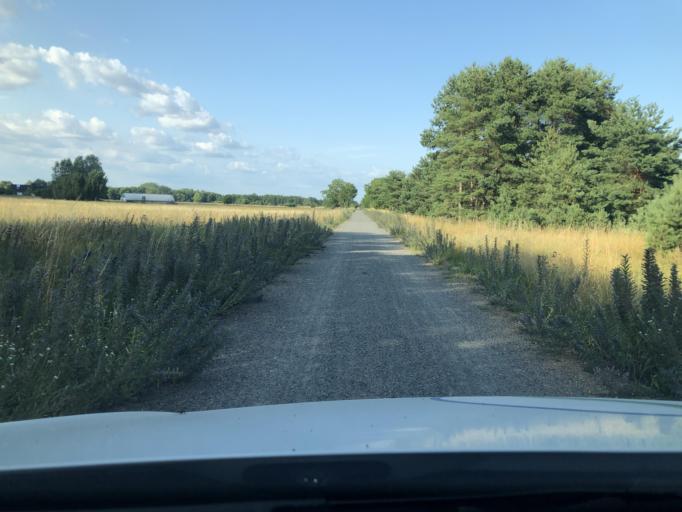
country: SE
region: Skane
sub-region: Kristianstads Kommun
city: Norra Asum
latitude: 55.9369
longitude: 14.1397
